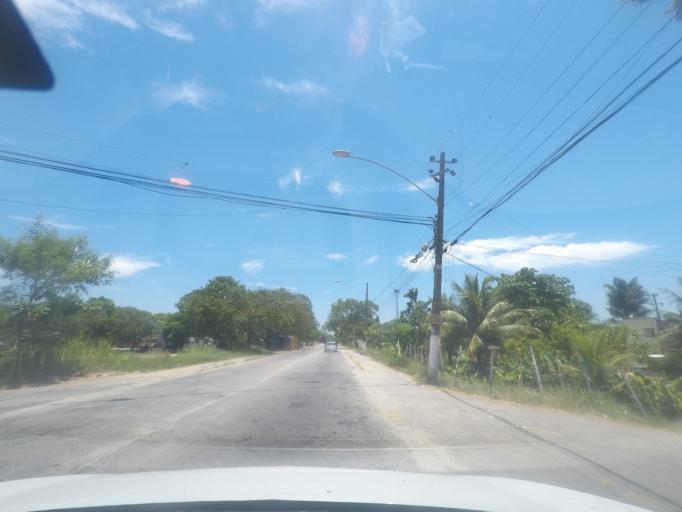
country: BR
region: Rio de Janeiro
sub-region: Itaguai
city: Itaguai
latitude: -22.9056
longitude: -43.6927
